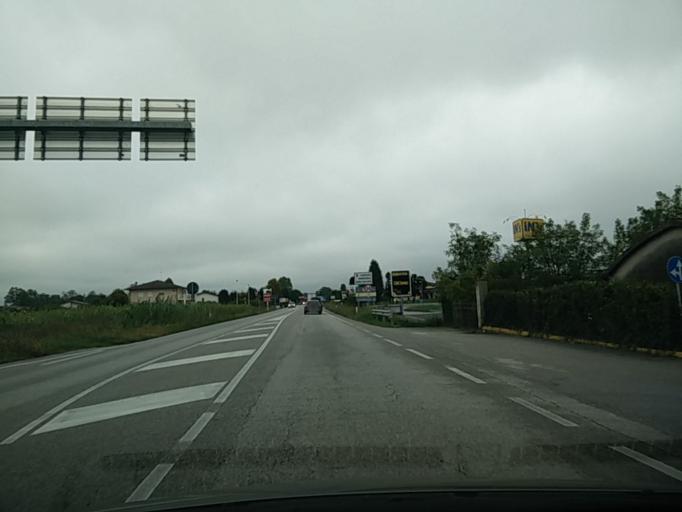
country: IT
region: Veneto
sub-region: Provincia di Treviso
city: Vedelago
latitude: 45.6850
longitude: 12.0006
